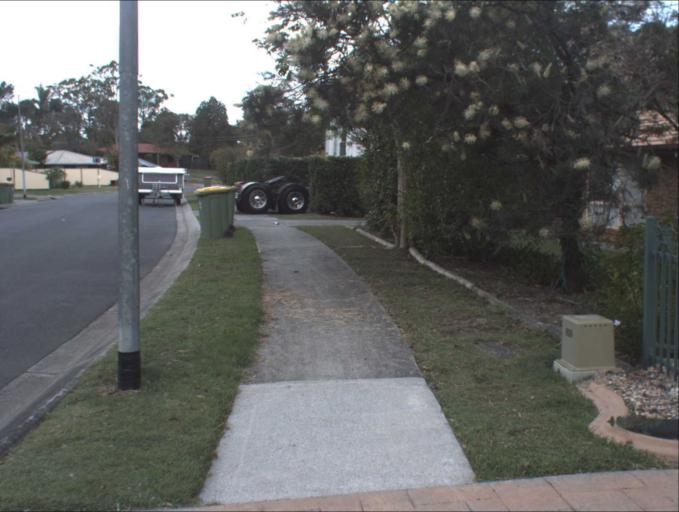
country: AU
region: Queensland
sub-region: Logan
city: Waterford West
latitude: -27.6822
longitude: 153.1301
